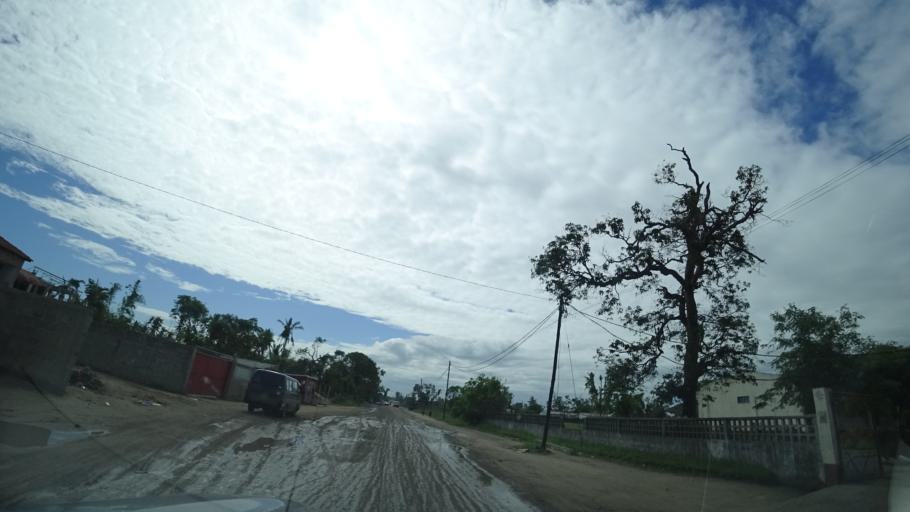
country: MZ
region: Sofala
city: Beira
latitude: -19.7677
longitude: 34.8678
